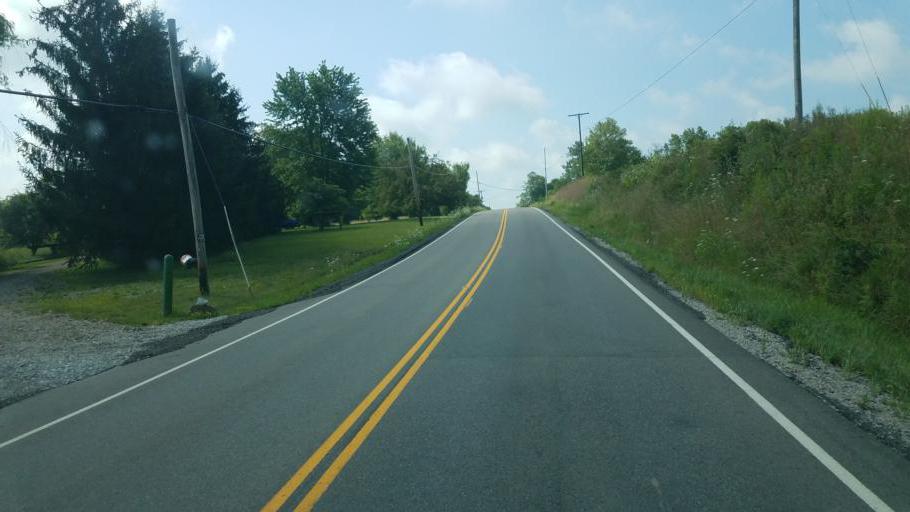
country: US
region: Ohio
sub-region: Knox County
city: Mount Vernon
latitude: 40.3335
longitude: -82.5076
